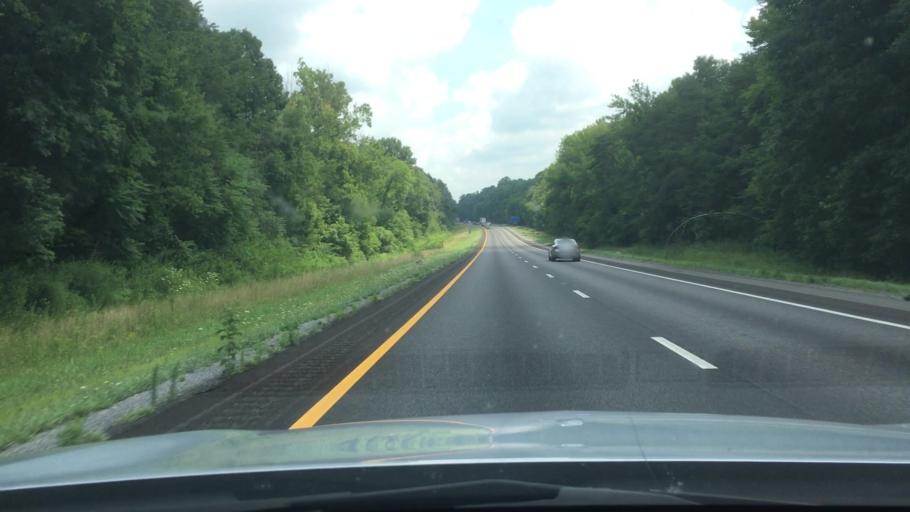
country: US
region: Tennessee
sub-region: McMinn County
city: Athens
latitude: 35.4085
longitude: -84.7033
